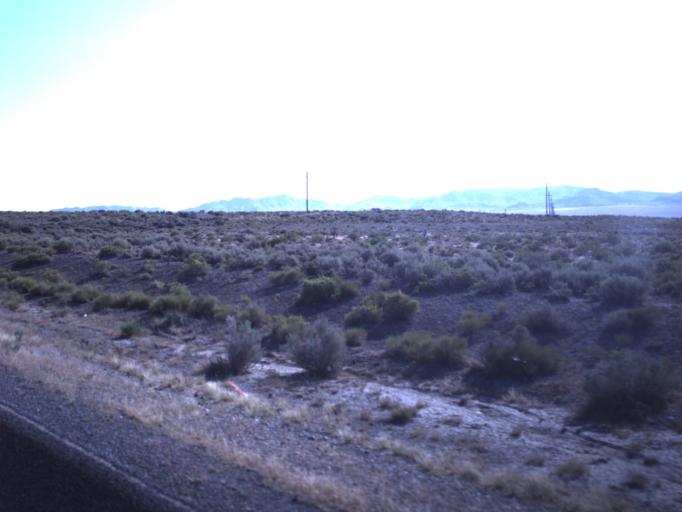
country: US
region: Utah
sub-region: Beaver County
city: Milford
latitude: 38.4589
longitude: -113.0046
